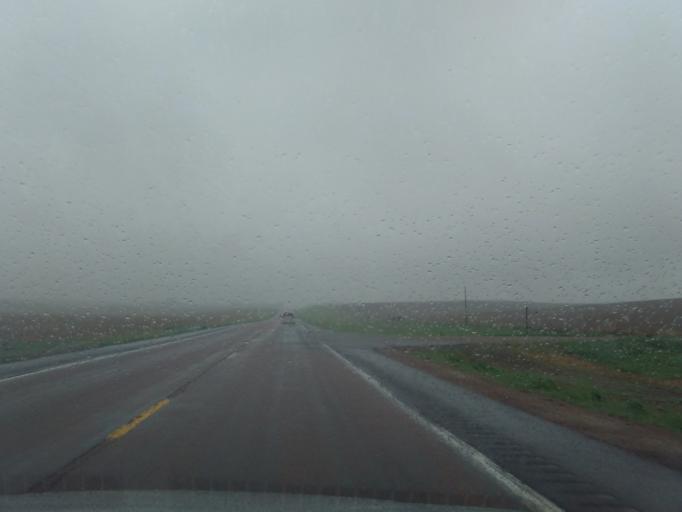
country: US
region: Nebraska
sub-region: Wayne County
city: Wayne
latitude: 42.2356
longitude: -97.1148
